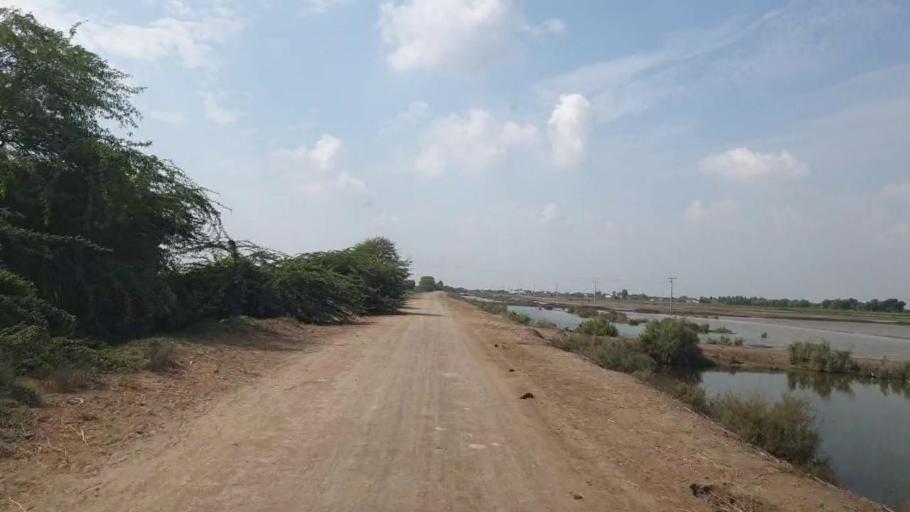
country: PK
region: Sindh
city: Badin
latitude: 24.5066
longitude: 68.6530
